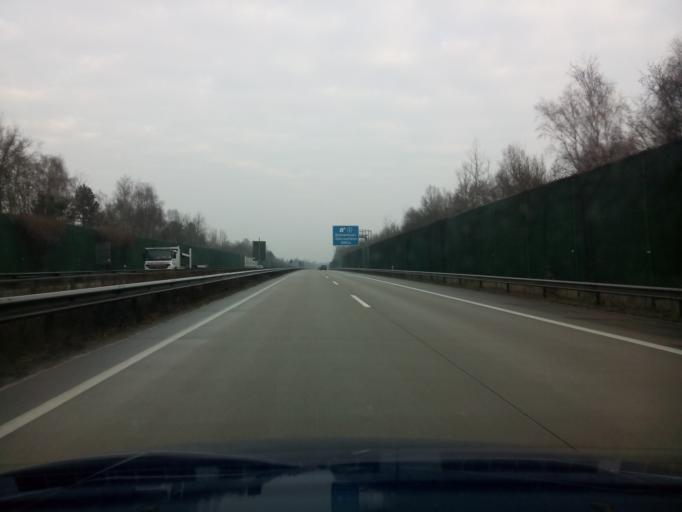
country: DE
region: Lower Saxony
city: Langen
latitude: 53.5689
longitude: 8.6198
